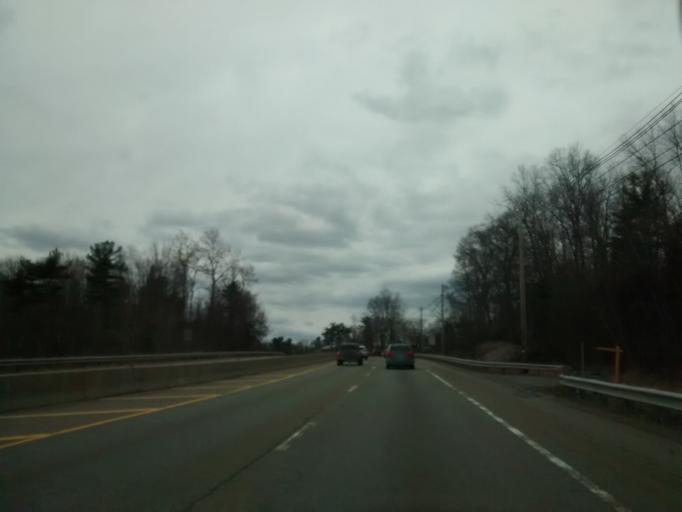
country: US
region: Massachusetts
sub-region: Worcester County
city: Charlton
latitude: 42.1475
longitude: -71.9435
